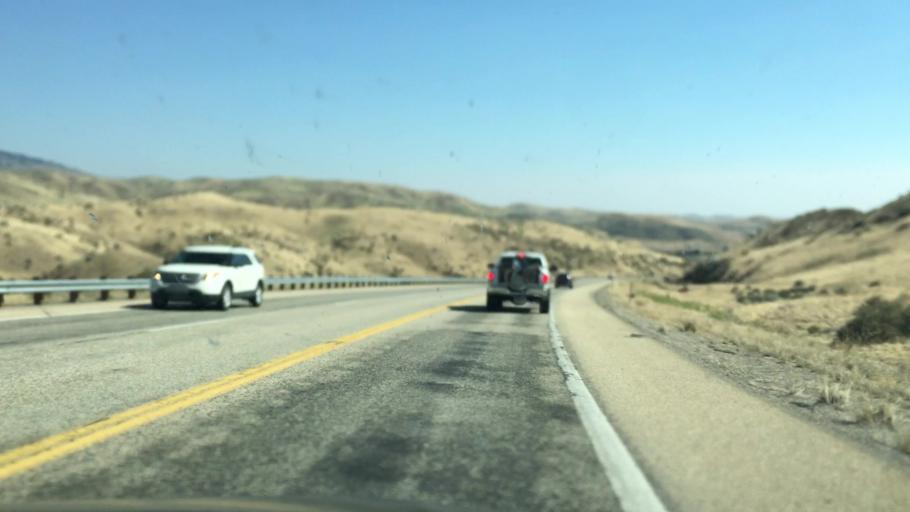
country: US
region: Idaho
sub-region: Ada County
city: Eagle
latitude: 43.8074
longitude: -116.2657
